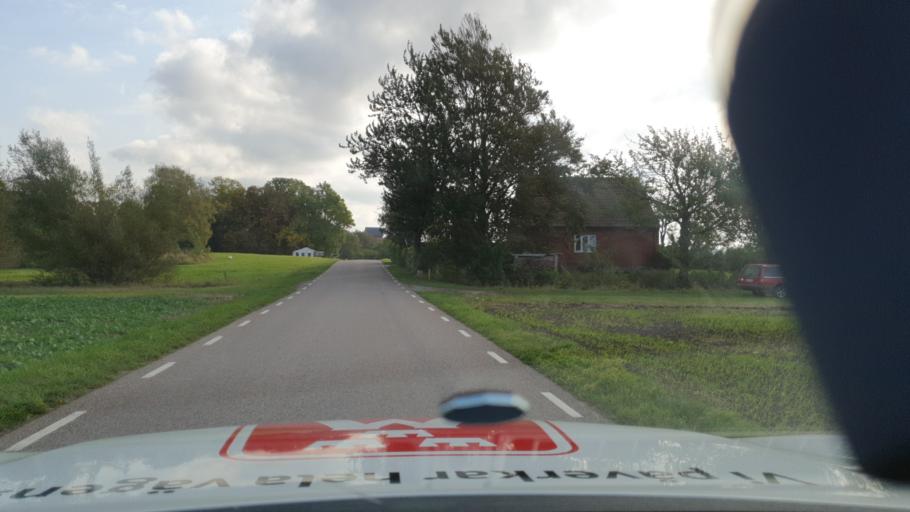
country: SE
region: Skane
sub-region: Malmo
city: Oxie
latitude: 55.4542
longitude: 13.1047
